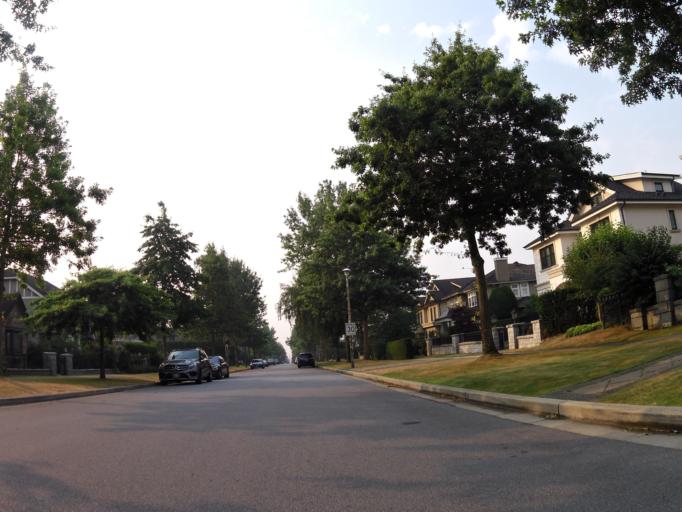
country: CA
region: British Columbia
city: Vancouver
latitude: 49.2217
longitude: -123.1482
